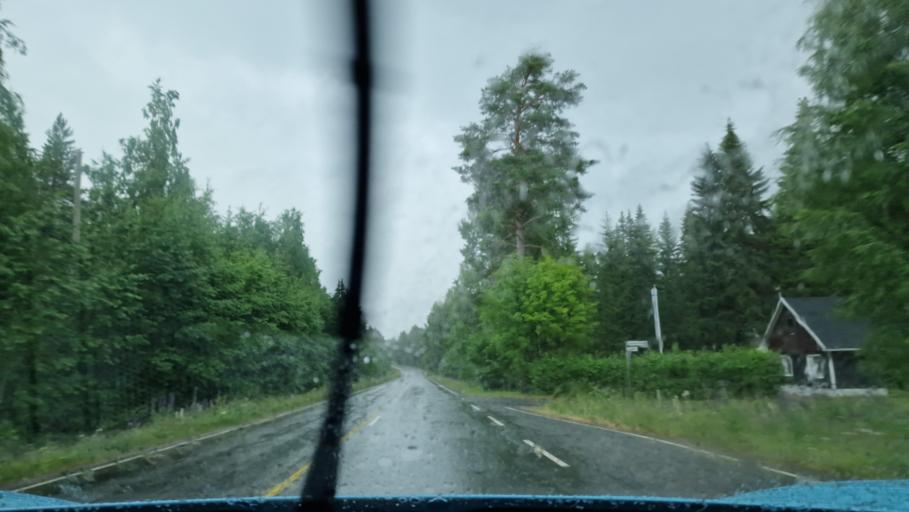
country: FI
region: Southern Ostrobothnia
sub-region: Jaerviseutu
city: Soini
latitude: 62.8206
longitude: 24.3482
